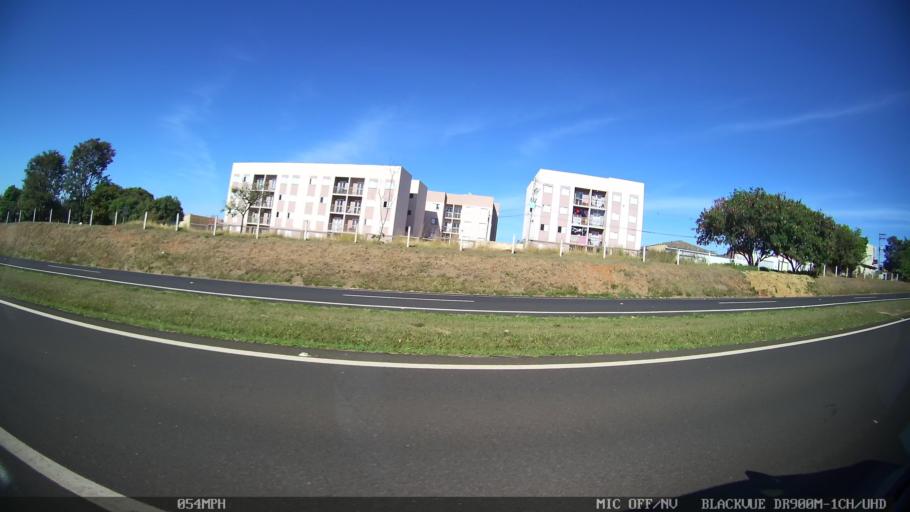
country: BR
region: Sao Paulo
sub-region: Franca
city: Franca
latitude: -20.5745
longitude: -47.3670
